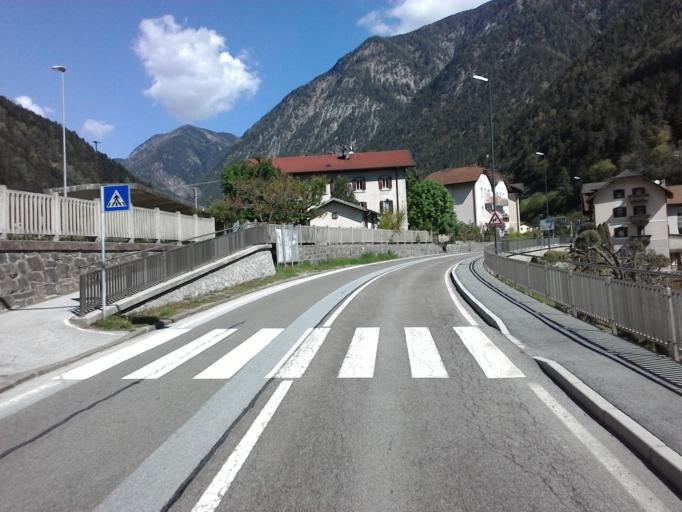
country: IT
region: Trentino-Alto Adige
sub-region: Bolzano
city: Fortezza
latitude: 46.7873
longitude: 11.6118
